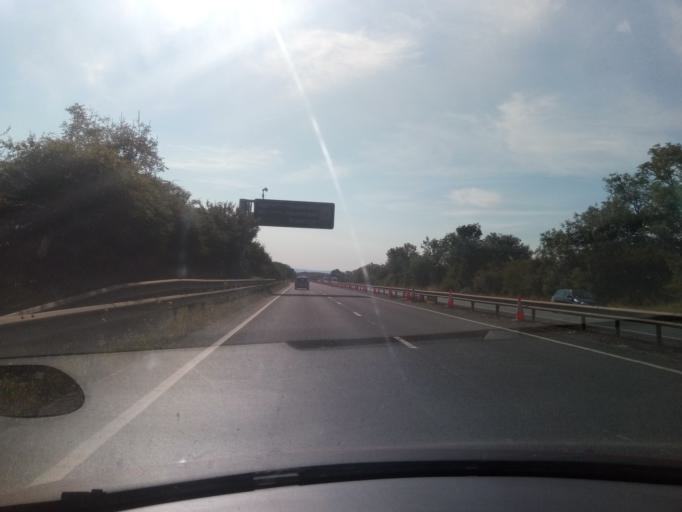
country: GB
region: England
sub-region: Hartlepool
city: Elwick
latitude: 54.6417
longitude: -1.2993
